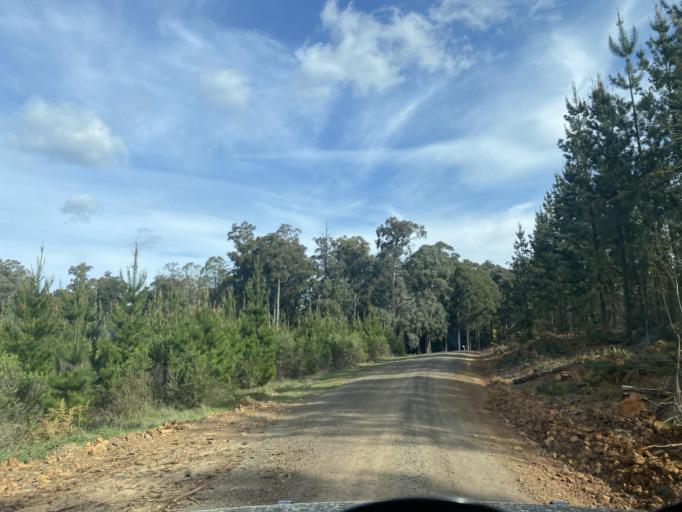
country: AU
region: Victoria
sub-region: Mansfield
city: Mansfield
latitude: -36.8409
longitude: 146.1830
